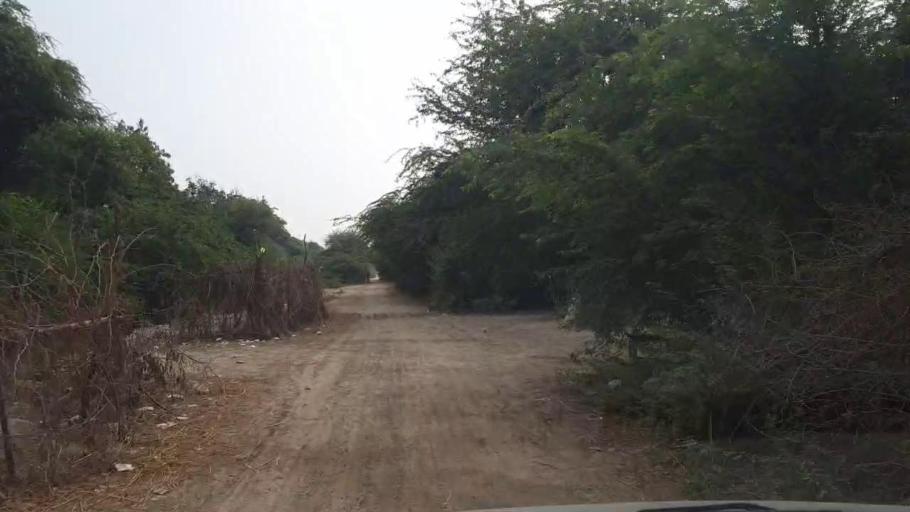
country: PK
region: Sindh
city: Matli
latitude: 24.9822
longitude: 68.7039
